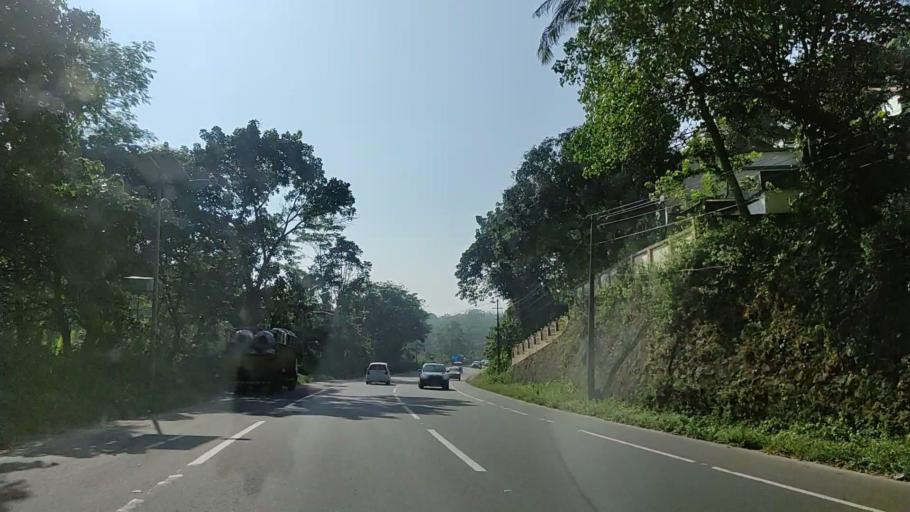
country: IN
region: Kerala
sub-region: Kollam
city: Punalur
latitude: 8.9119
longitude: 76.8543
